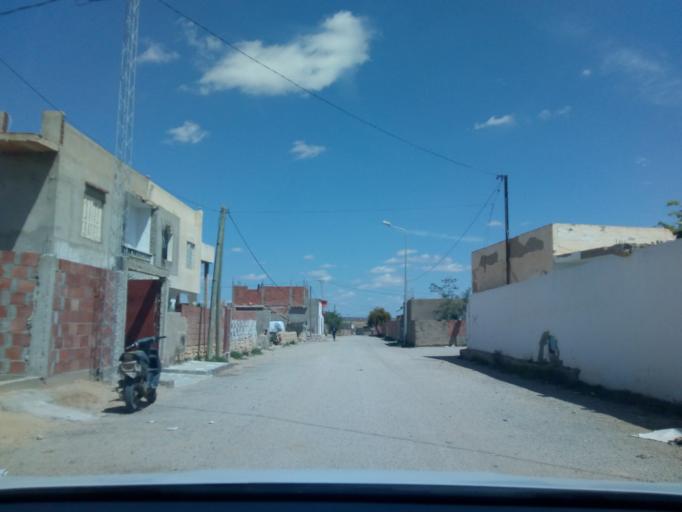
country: TN
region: Safaqis
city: Sfax
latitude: 34.7294
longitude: 10.4916
